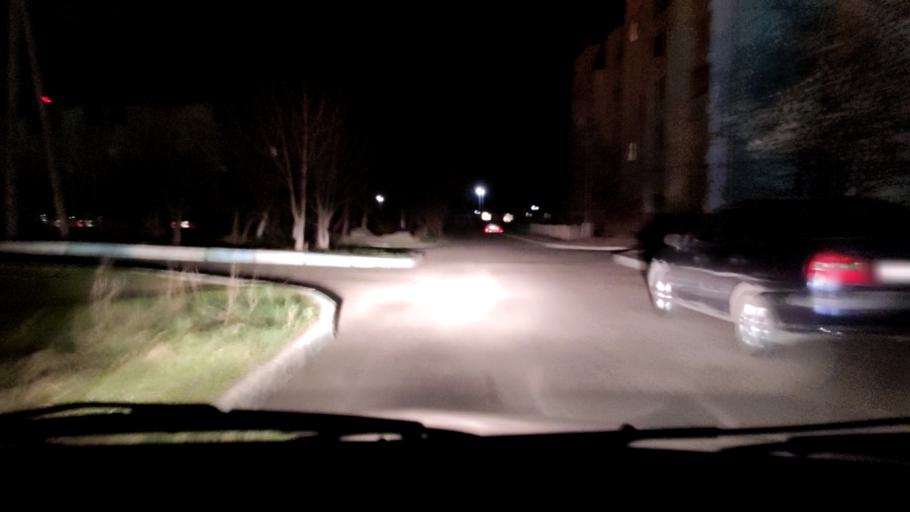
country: RU
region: Voronezj
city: Novaya Usman'
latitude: 51.6100
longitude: 39.3720
